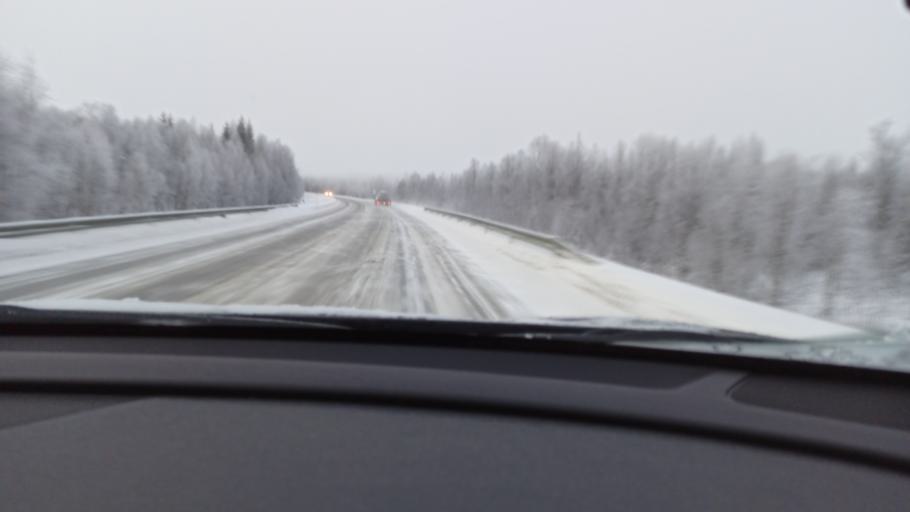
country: FI
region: Lapland
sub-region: Pohjois-Lappi
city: Sodankylae
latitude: 66.9272
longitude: 26.2177
